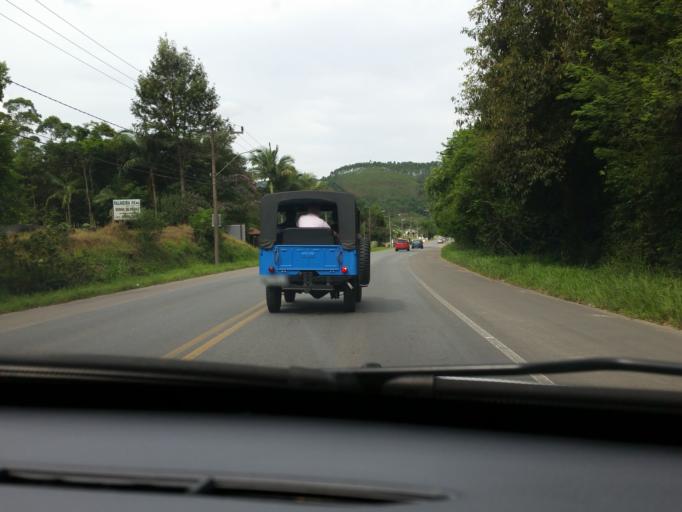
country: BR
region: Santa Catarina
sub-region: Rodeio
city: Gavea
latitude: -27.0276
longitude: -49.3803
